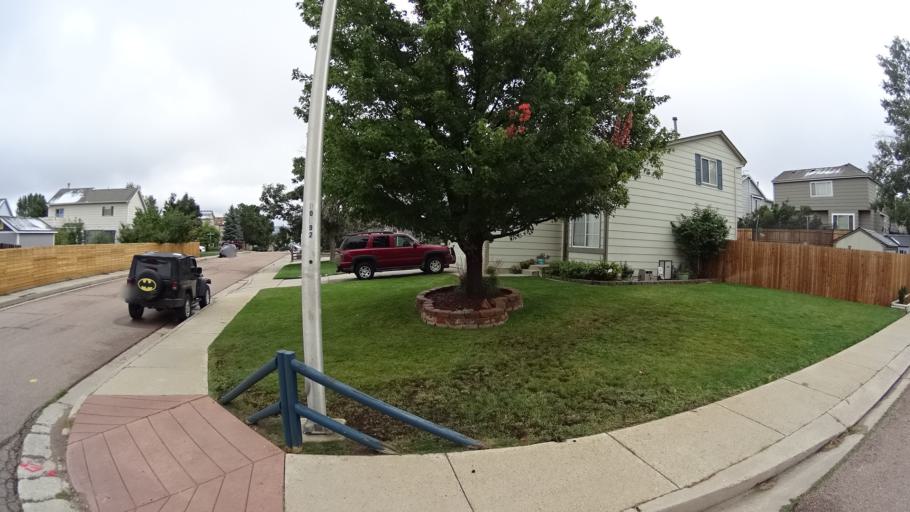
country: US
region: Colorado
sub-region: El Paso County
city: Cimarron Hills
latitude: 38.9186
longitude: -104.7550
